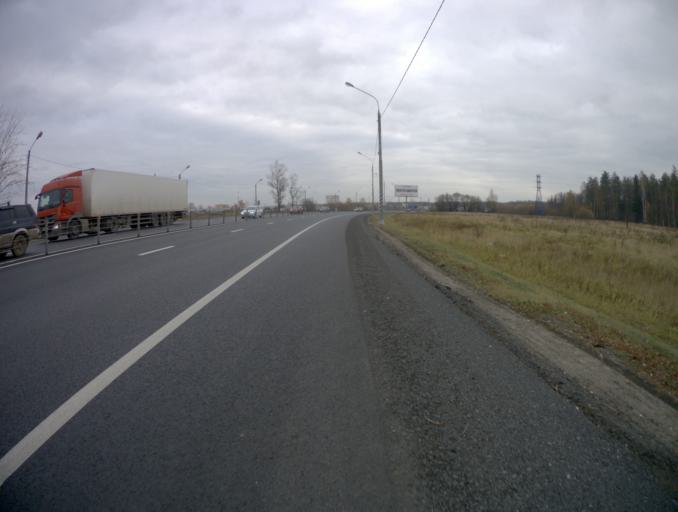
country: RU
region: Moskovskaya
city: Malaya Dubna
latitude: 55.8717
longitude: 38.9632
